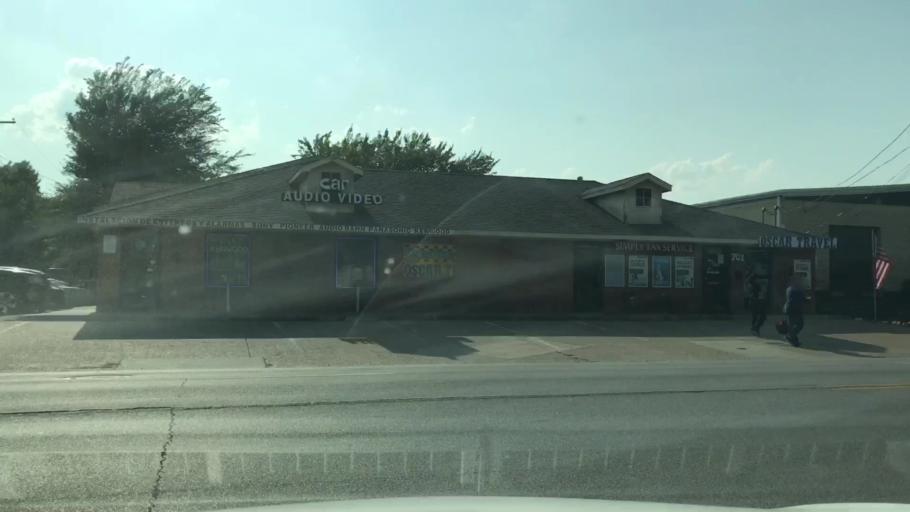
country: US
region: Texas
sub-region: Dallas County
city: Irving
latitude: 32.8200
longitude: -96.9423
